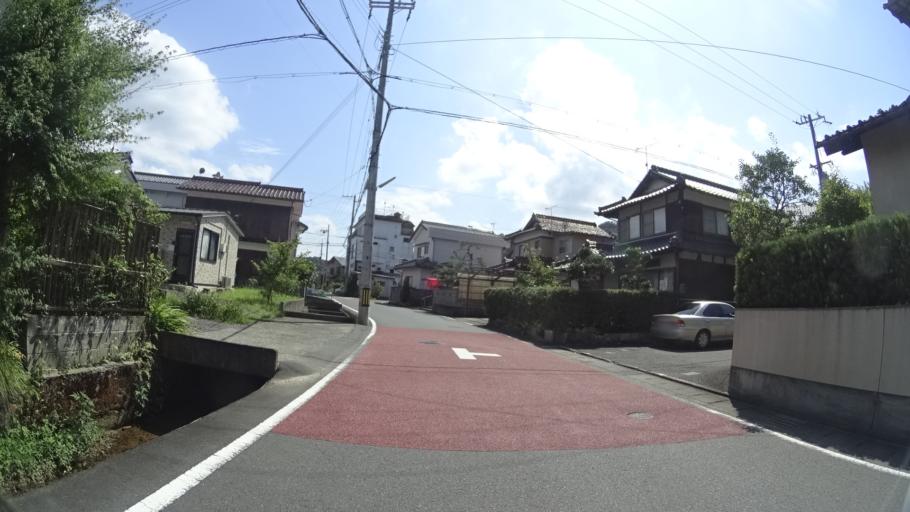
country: JP
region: Kyoto
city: Maizuru
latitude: 35.4411
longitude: 135.3246
